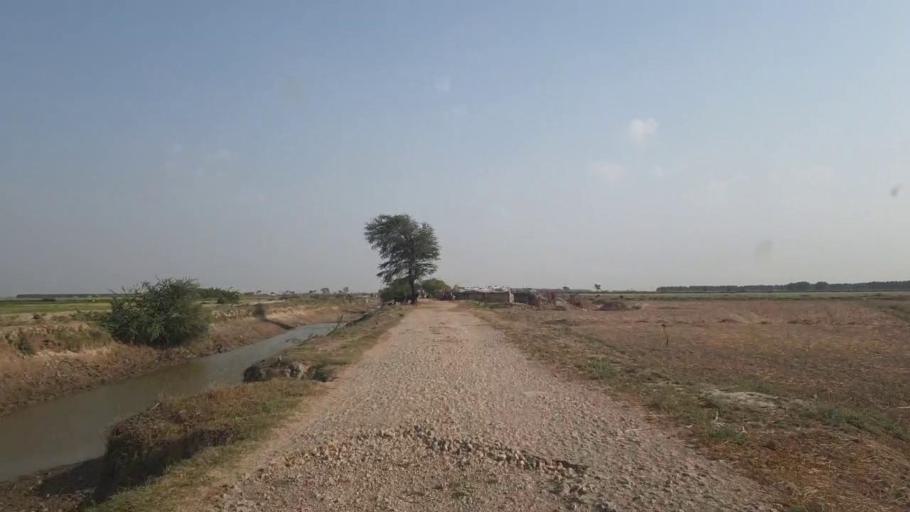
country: PK
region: Sindh
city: Kario
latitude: 24.5926
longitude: 68.5559
